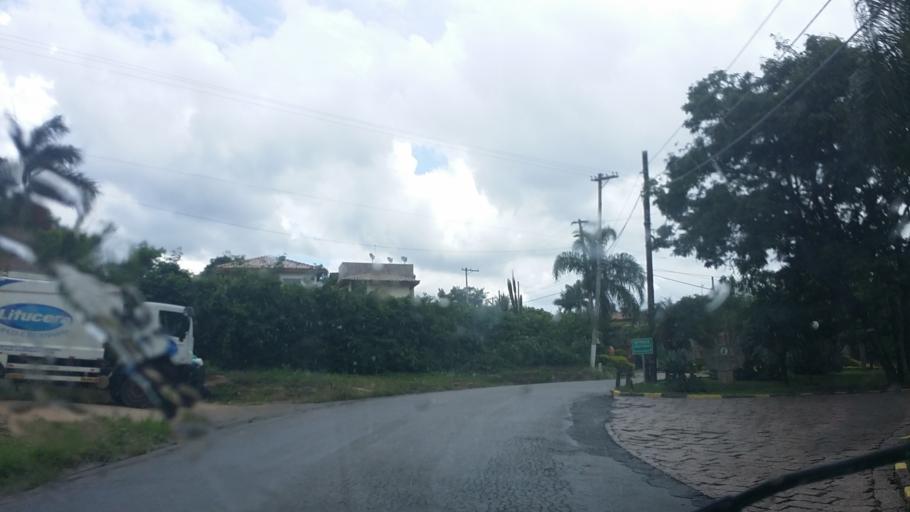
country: BR
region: Sao Paulo
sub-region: Itupeva
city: Itupeva
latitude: -23.1700
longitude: -47.1079
